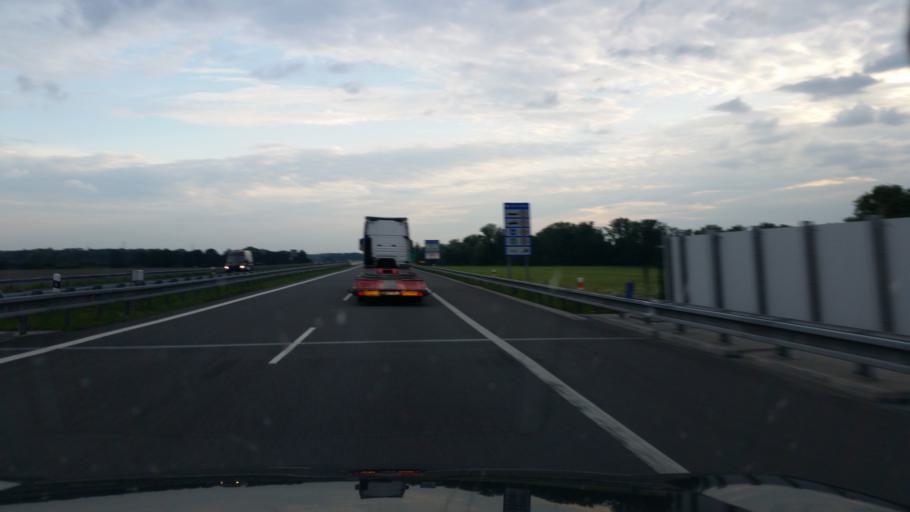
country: PL
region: Silesian Voivodeship
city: Gorzyczki
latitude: 49.9345
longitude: 18.4030
